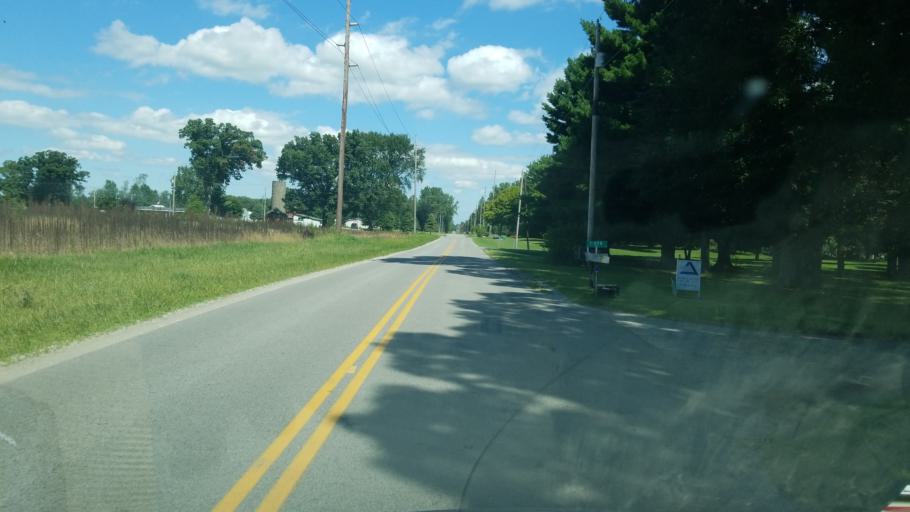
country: US
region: Ohio
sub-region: Henry County
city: Liberty Center
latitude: 41.4568
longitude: -83.9214
